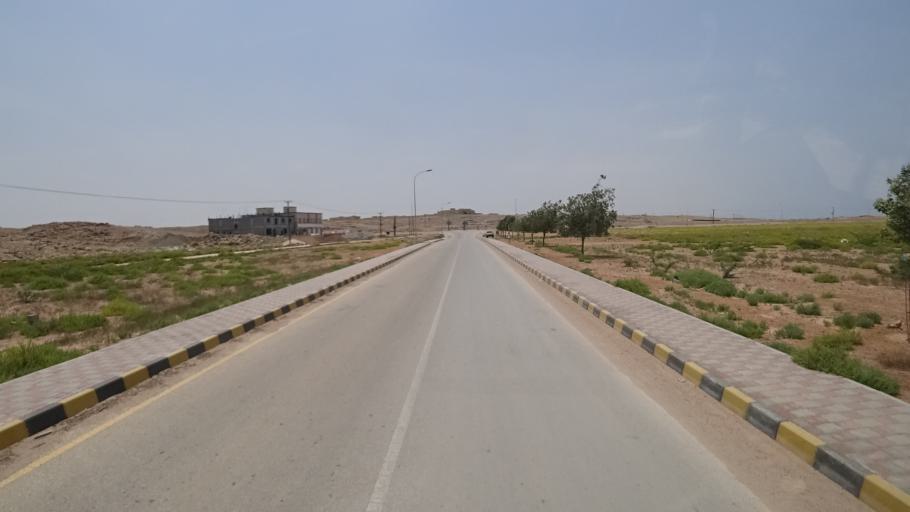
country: OM
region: Ash Sharqiyah
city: Sur
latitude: 22.5098
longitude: 59.7971
